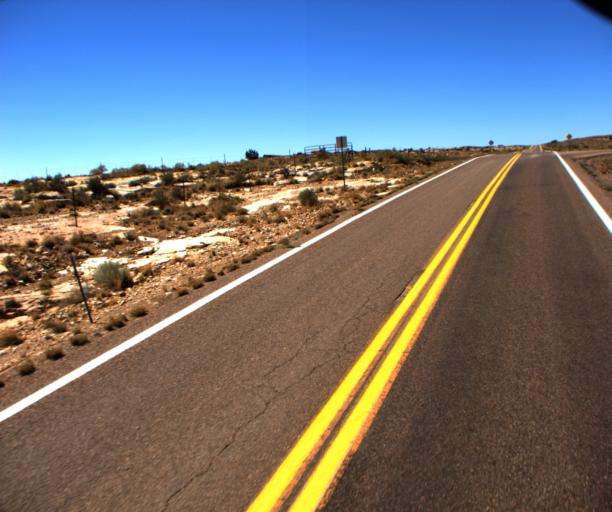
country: US
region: Arizona
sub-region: Navajo County
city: Winslow
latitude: 34.9667
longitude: -110.6466
